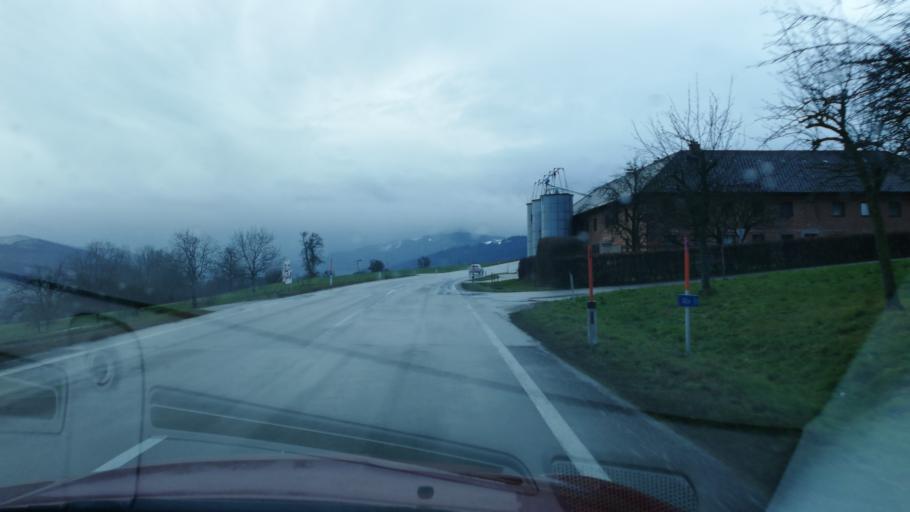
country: AT
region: Upper Austria
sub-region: Politischer Bezirk Kirchdorf an der Krems
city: Kremsmunster
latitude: 47.9755
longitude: 14.0785
